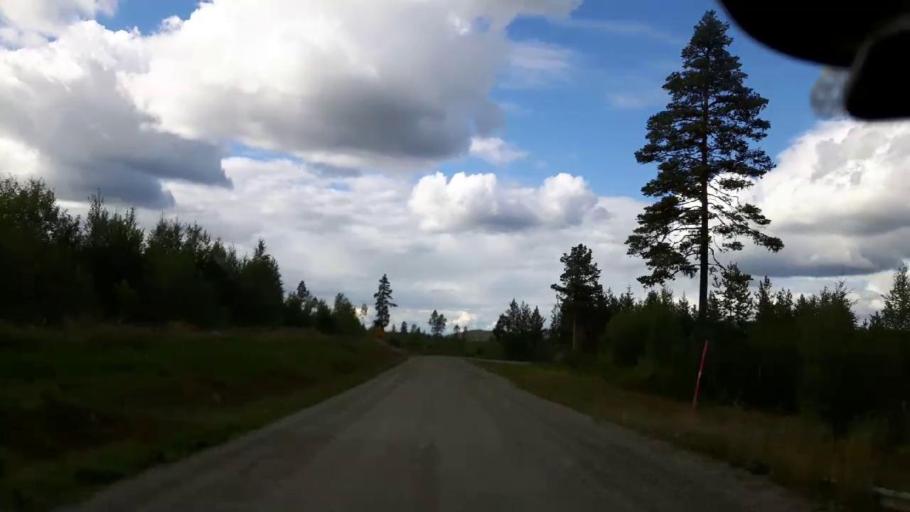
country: SE
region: Jaemtland
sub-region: Stroemsunds Kommun
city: Stroemsund
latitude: 63.4040
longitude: 15.5683
